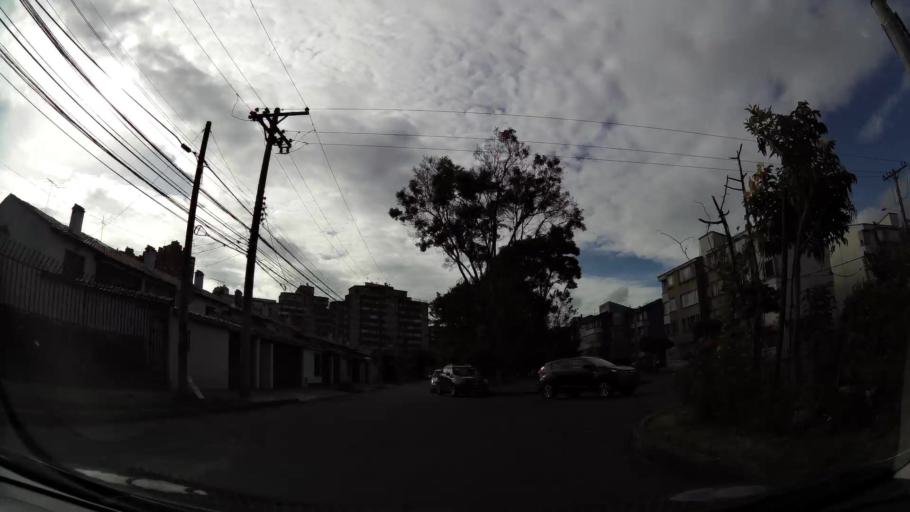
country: CO
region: Bogota D.C.
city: Barrio San Luis
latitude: 4.6909
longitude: -74.0726
